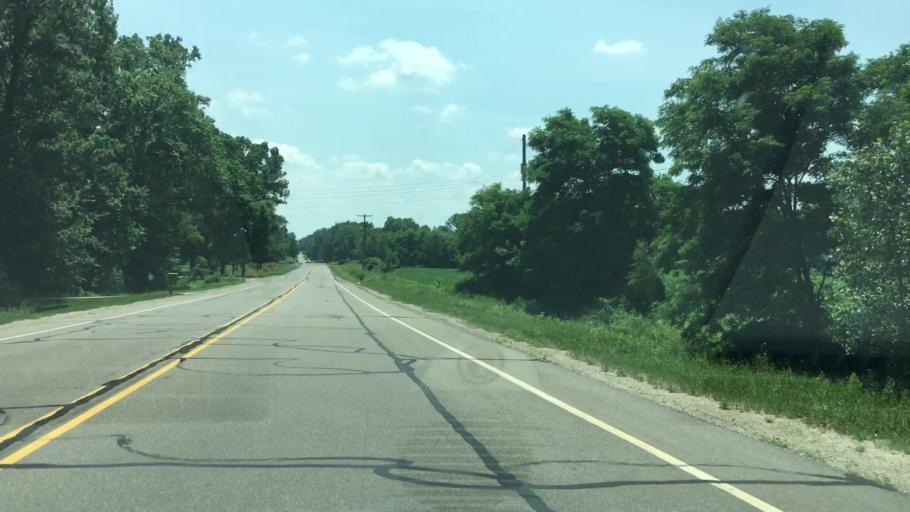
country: US
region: Michigan
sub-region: Kent County
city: Byron Center
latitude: 42.8437
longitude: -85.7628
